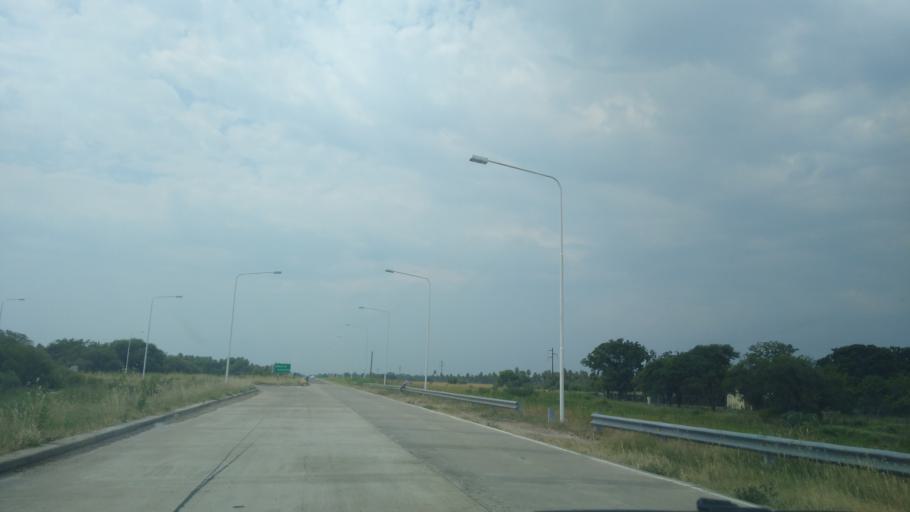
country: AR
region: Chaco
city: Margarita Belen
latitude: -27.0869
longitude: -58.9565
